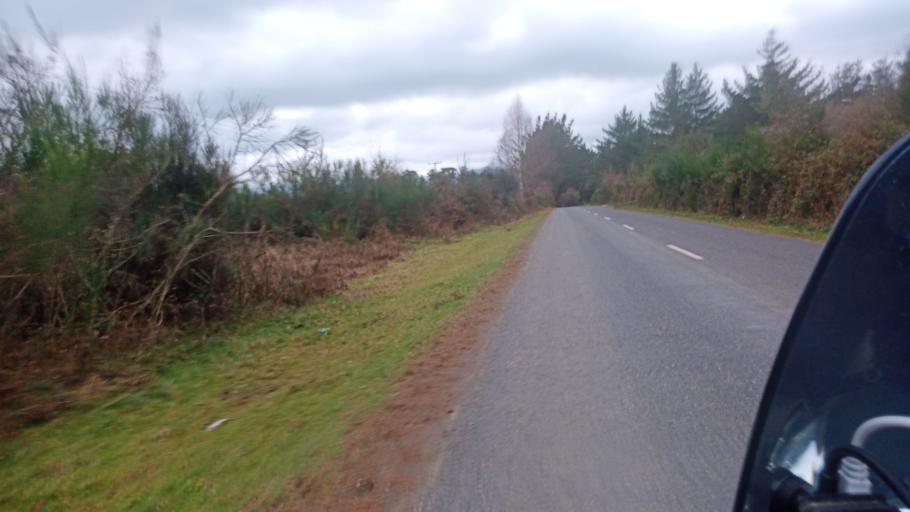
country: NZ
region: Bay of Plenty
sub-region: Whakatane District
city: Murupara
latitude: -38.6397
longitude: 176.7274
